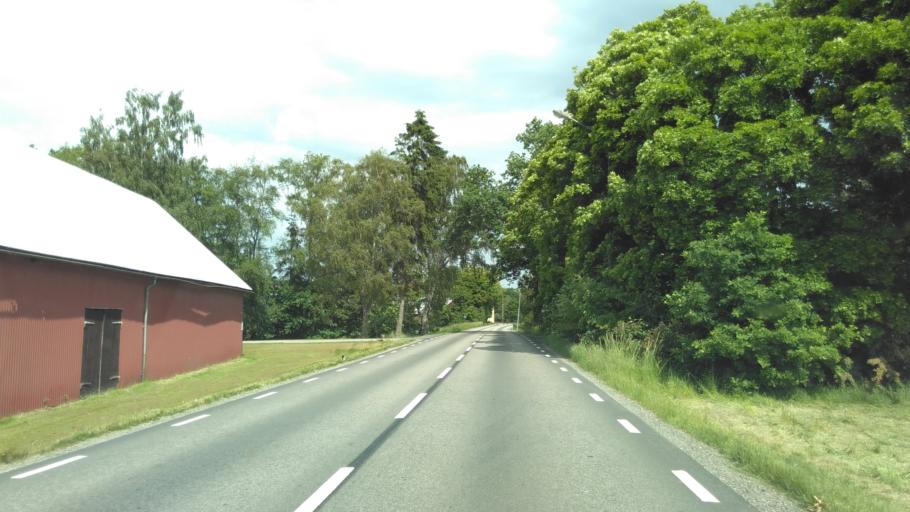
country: SE
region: Vaestra Goetaland
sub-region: Vara Kommun
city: Kvanum
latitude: 58.3710
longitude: 13.1475
